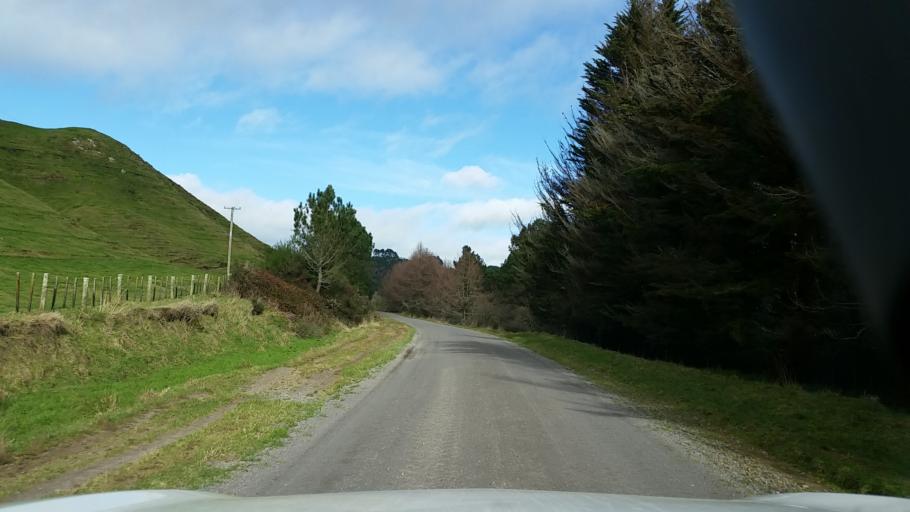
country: NZ
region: Waikato
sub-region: Taupo District
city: Taupo
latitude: -38.4583
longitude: 176.2415
